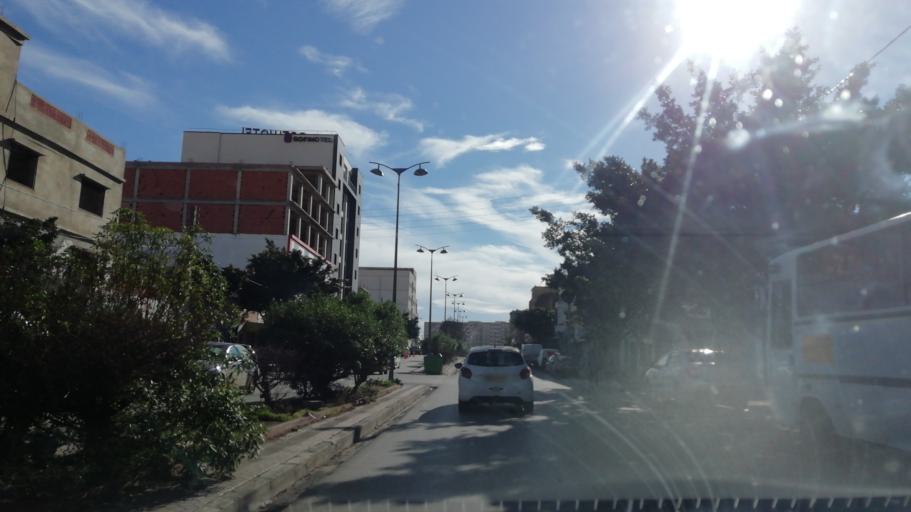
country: DZ
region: Oran
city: Oran
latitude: 35.6937
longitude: -0.6201
